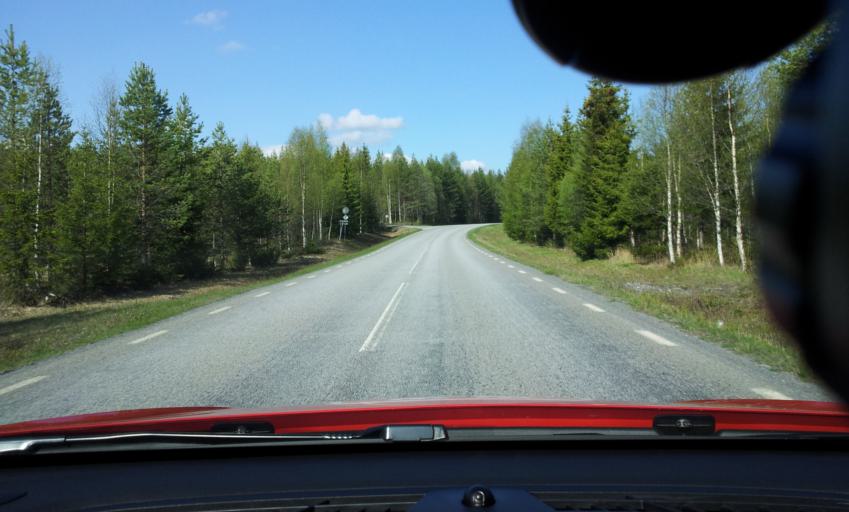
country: SE
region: Jaemtland
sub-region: Krokoms Kommun
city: Krokom
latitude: 63.1288
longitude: 14.2219
